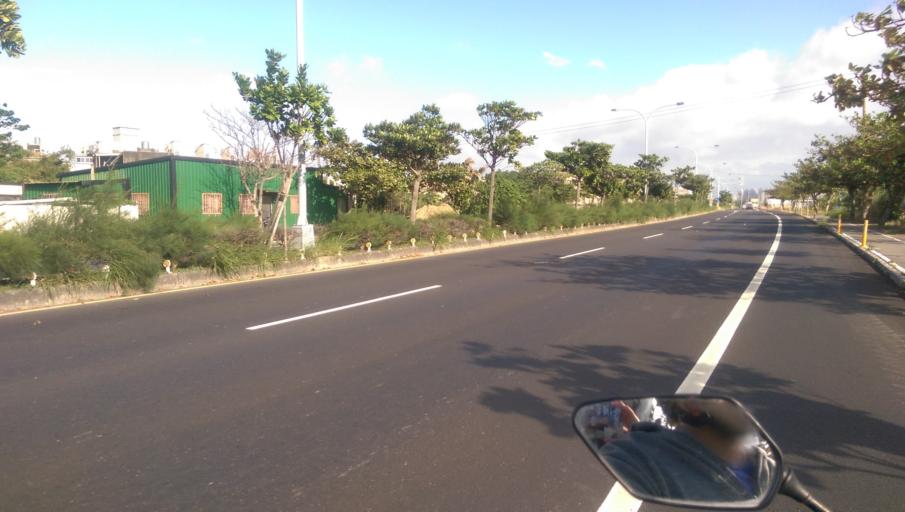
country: TW
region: Taiwan
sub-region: Hsinchu
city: Hsinchu
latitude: 24.8363
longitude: 120.9394
